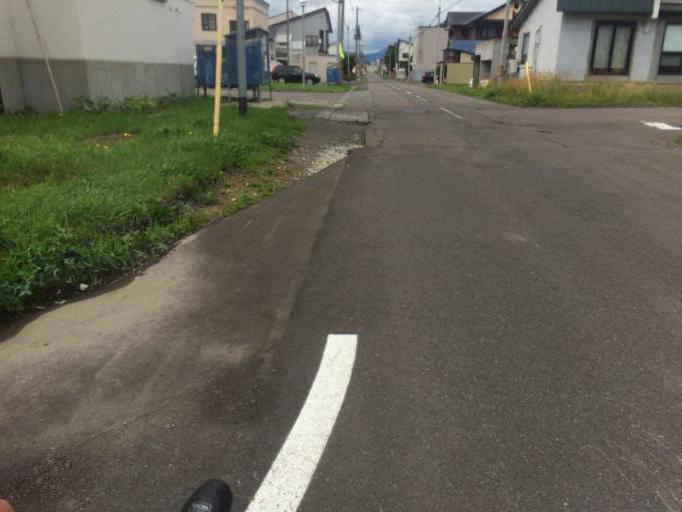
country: JP
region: Hokkaido
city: Niseko Town
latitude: 42.8903
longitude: 140.7509
